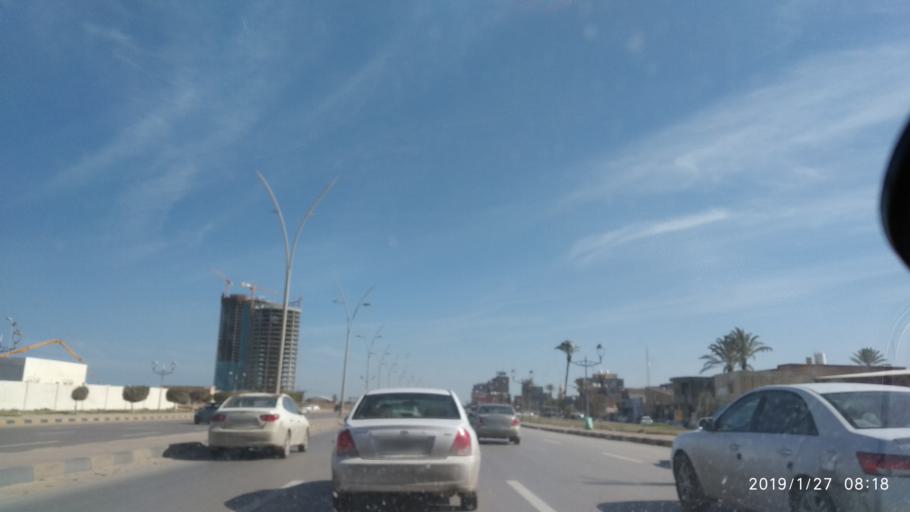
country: LY
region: Tripoli
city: Tripoli
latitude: 32.9065
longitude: 13.2594
